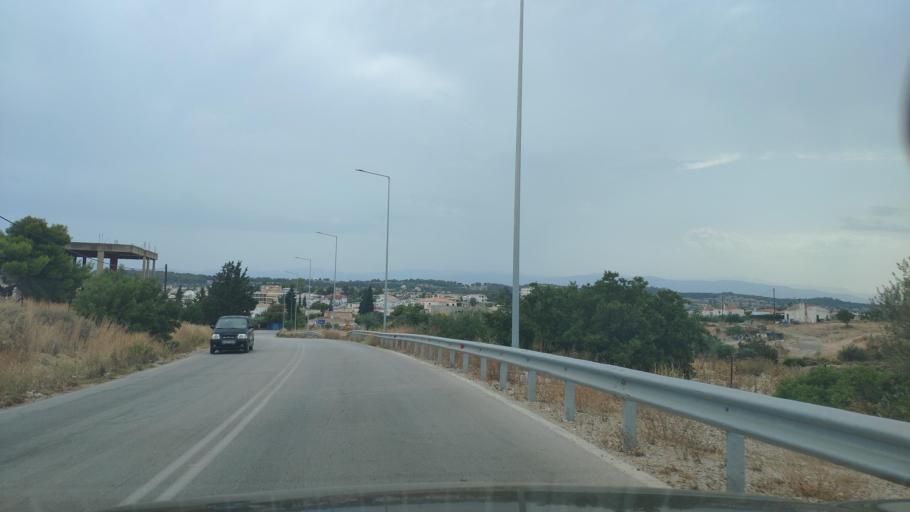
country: GR
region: Peloponnese
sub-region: Nomos Argolidos
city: Porto Cheli
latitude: 37.3319
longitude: 23.1488
